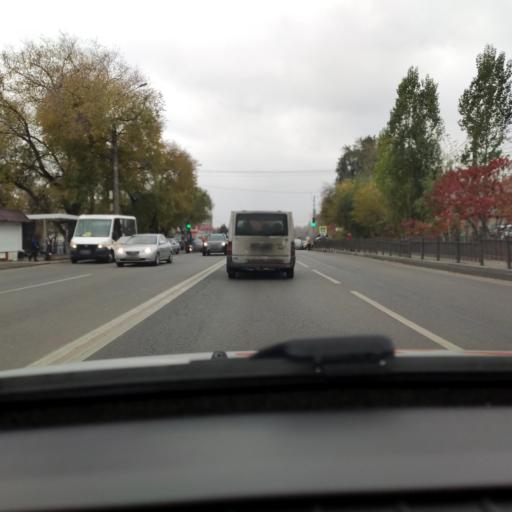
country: RU
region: Voronezj
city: Voronezh
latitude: 51.7002
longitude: 39.2325
